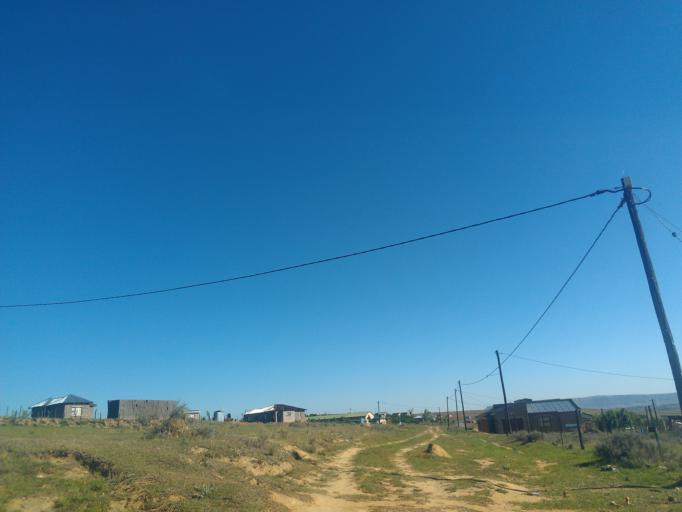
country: LS
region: Berea
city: Teyateyaneng
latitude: -29.1302
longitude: 27.7637
